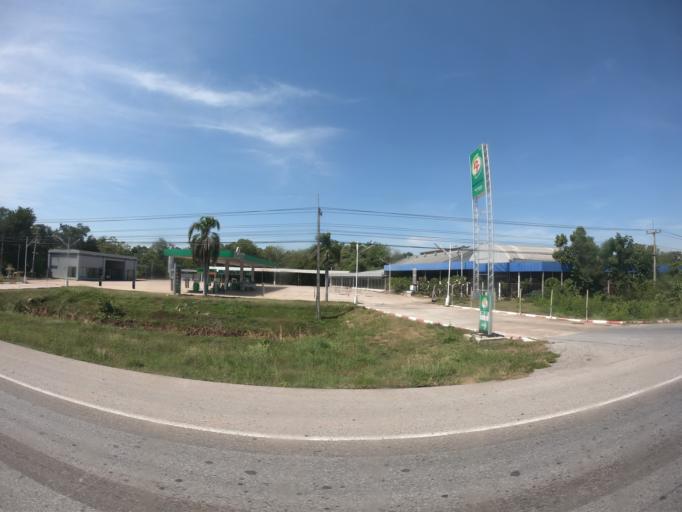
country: TH
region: Nakhon Ratchasima
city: Sida
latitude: 15.5314
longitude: 102.5440
